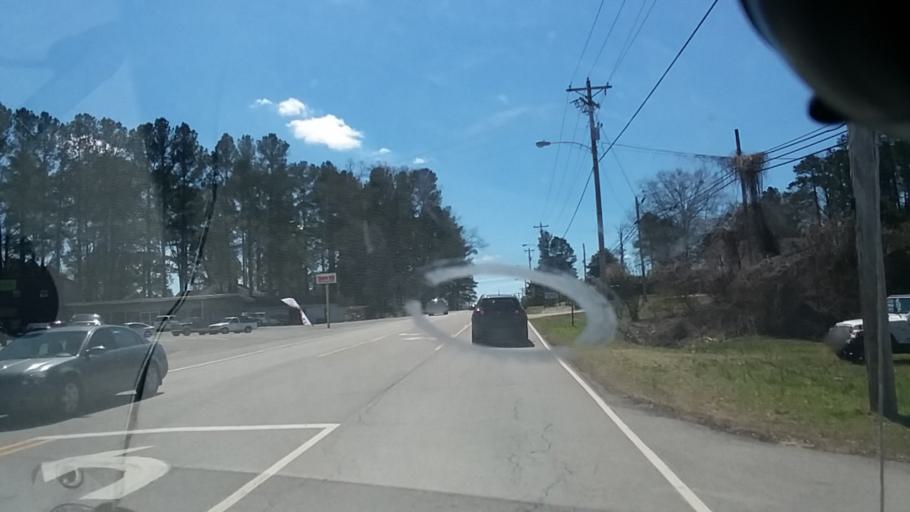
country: US
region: Mississippi
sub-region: Tishomingo County
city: Iuka
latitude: 34.8081
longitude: -88.2004
